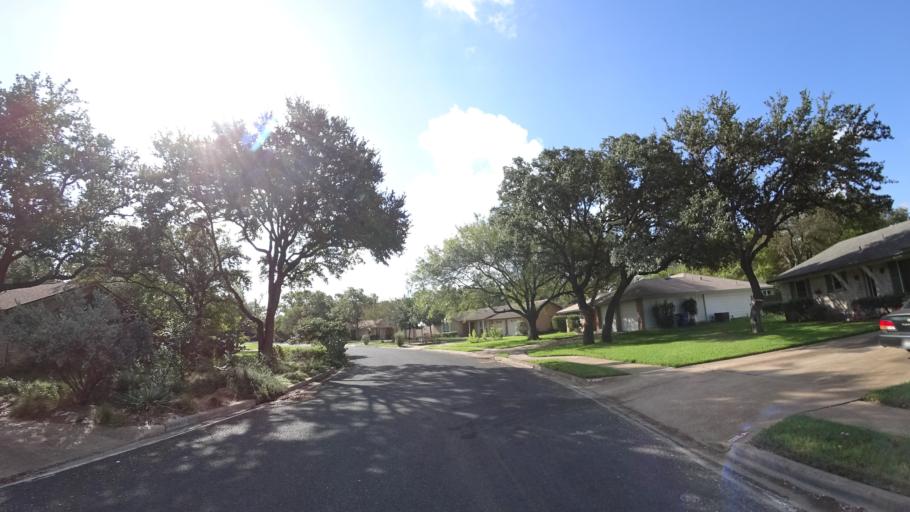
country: US
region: Texas
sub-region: Travis County
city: Rollingwood
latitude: 30.2163
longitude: -97.8032
